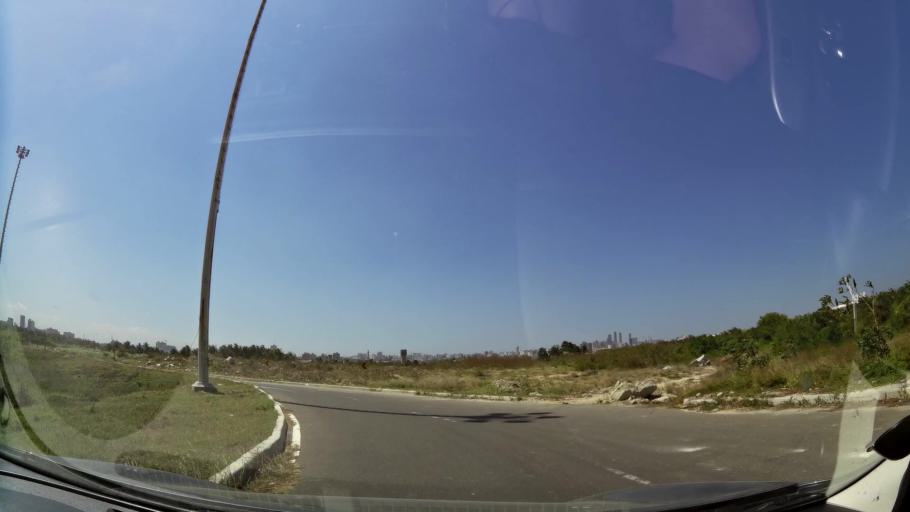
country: CO
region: Atlantico
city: Barranquilla
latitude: 10.9986
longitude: -74.7729
